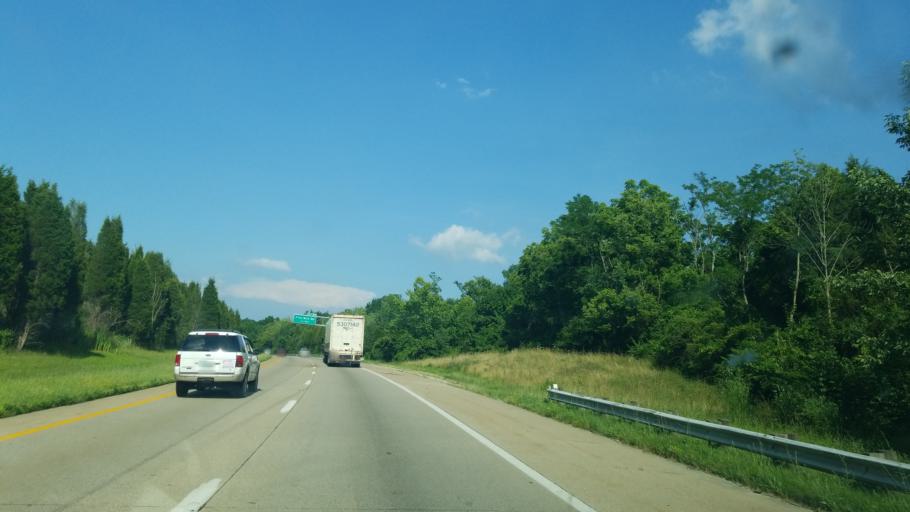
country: US
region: Ohio
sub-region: Hamilton County
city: Salem Heights
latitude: 39.0549
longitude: -84.3712
